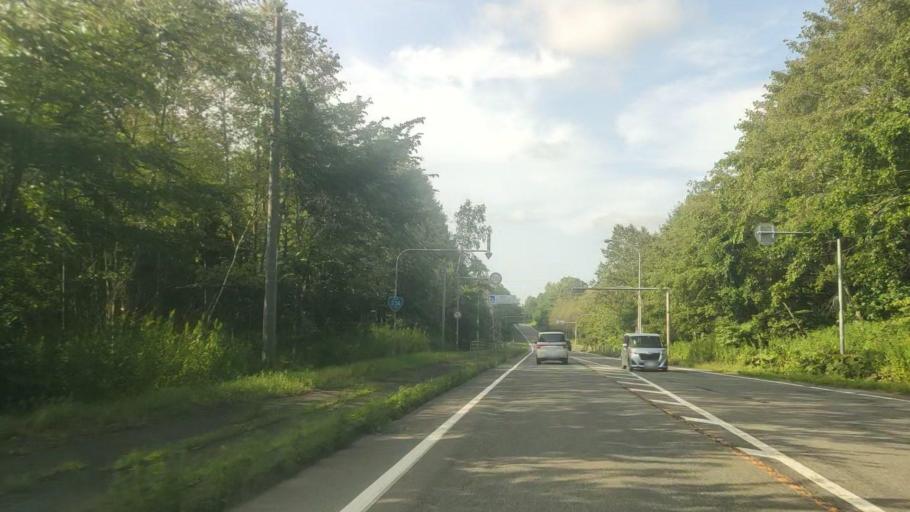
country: JP
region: Hokkaido
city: Chitose
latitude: 42.8669
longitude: 141.8226
